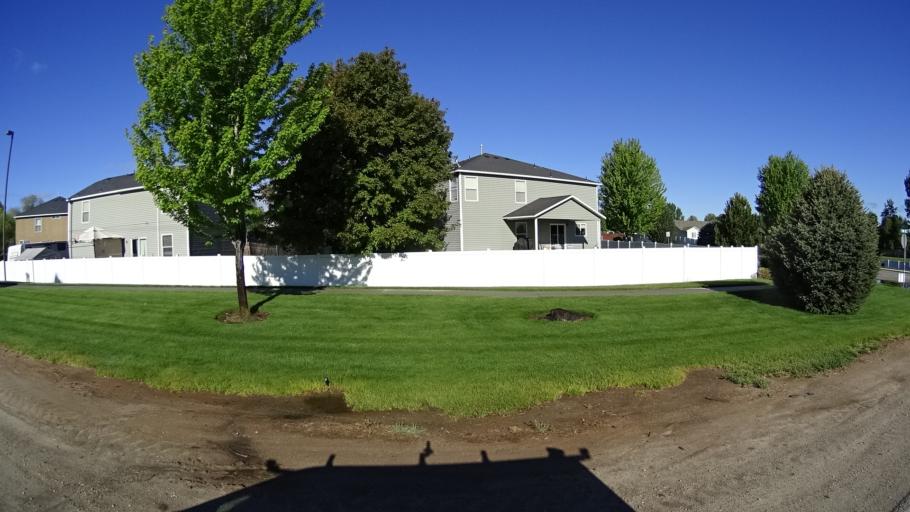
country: US
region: Idaho
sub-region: Ada County
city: Kuna
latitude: 43.4810
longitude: -116.4134
